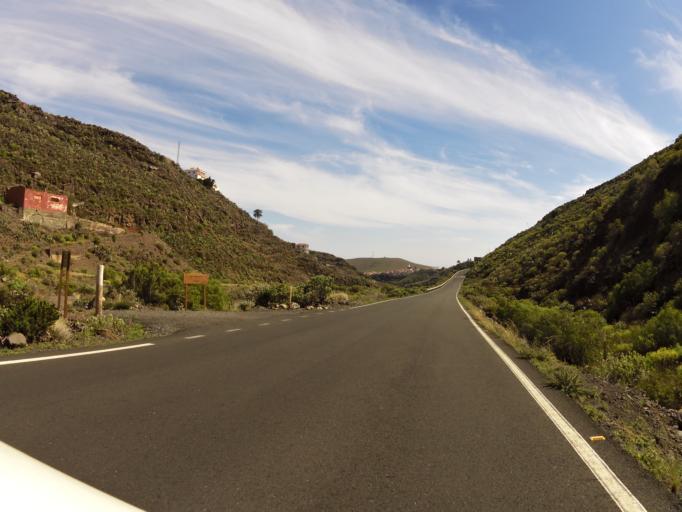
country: ES
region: Canary Islands
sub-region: Provincia de Las Palmas
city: Aguimes
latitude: 27.9174
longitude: -15.4557
